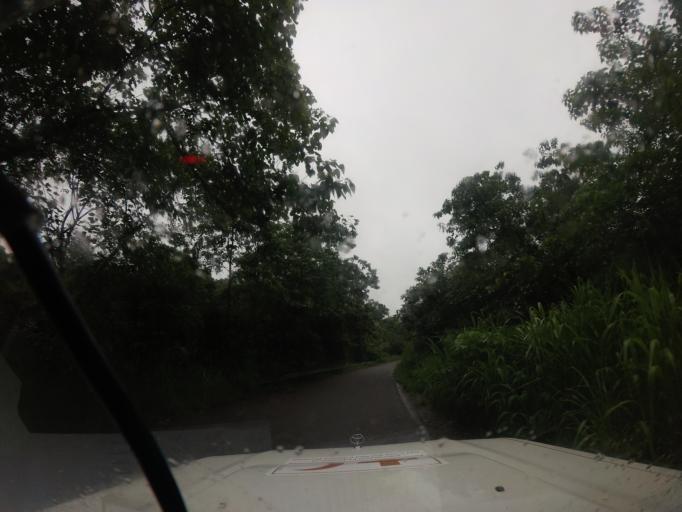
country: SL
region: Northern Province
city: Kabala
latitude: 9.4738
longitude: -11.6663
